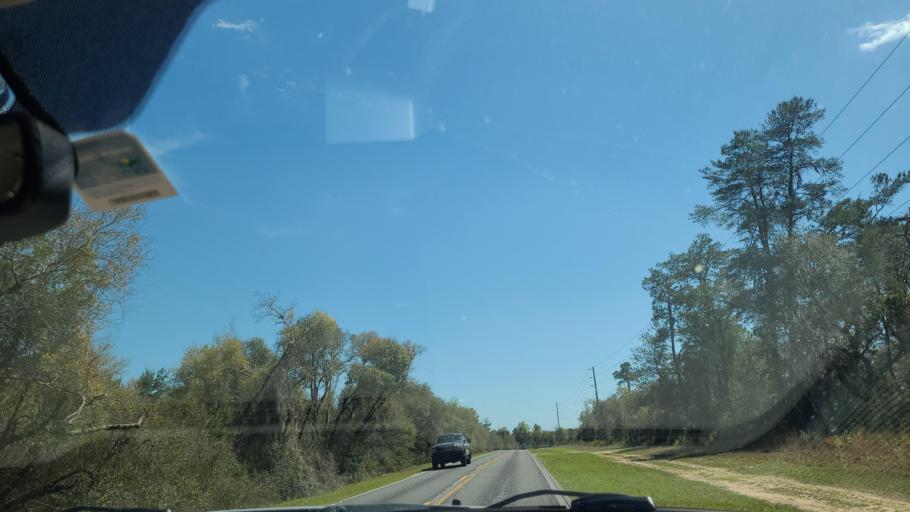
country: US
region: Florida
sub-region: Marion County
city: Citra
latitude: 29.4200
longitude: -81.9131
